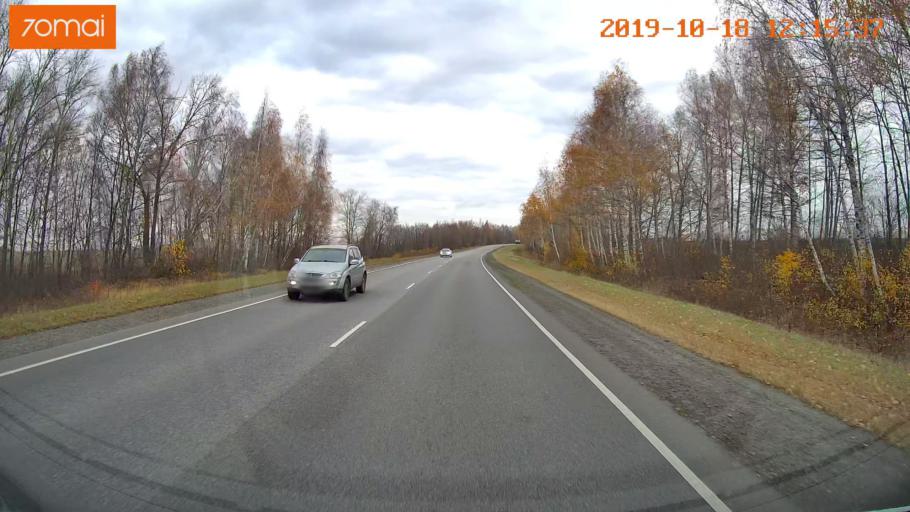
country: RU
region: Rjazan
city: Zakharovo
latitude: 54.4457
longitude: 39.4034
